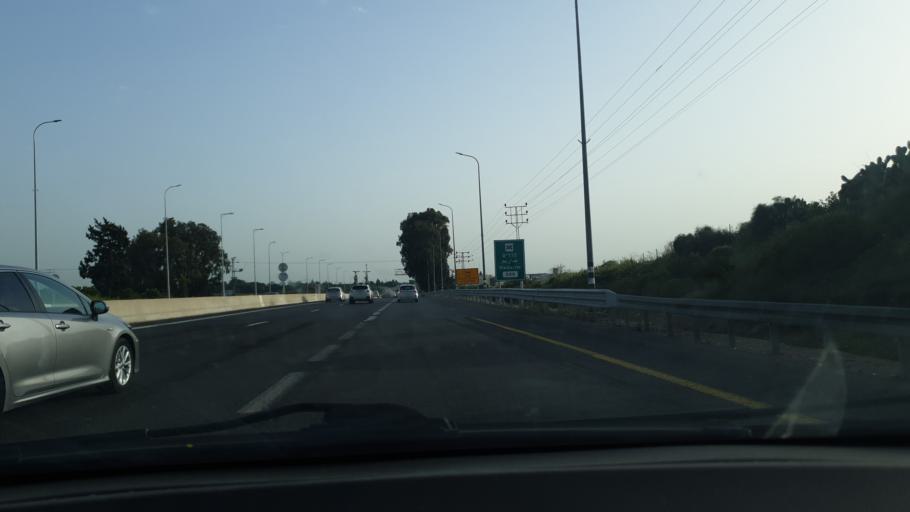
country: IL
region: Central District
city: Even Yehuda
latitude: 32.2482
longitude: 34.8890
